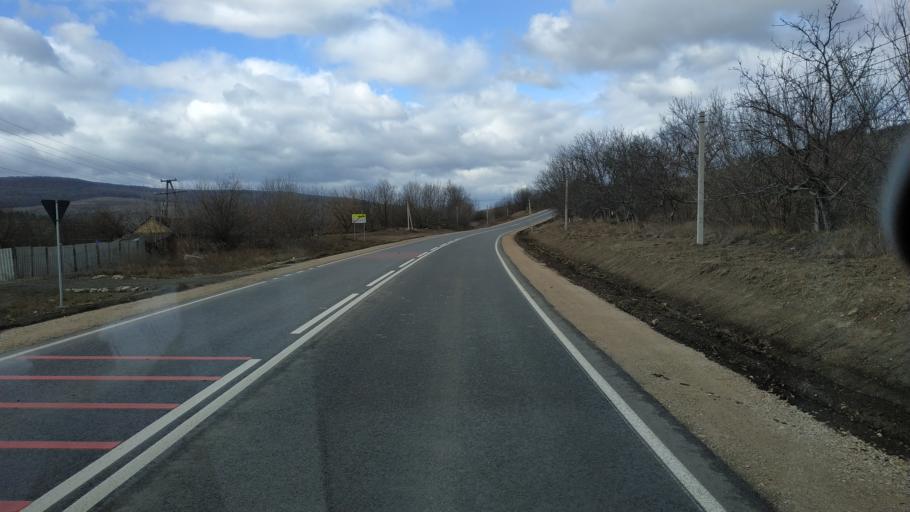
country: MD
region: Stinga Nistrului
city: Bucovat
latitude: 47.1909
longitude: 28.4434
